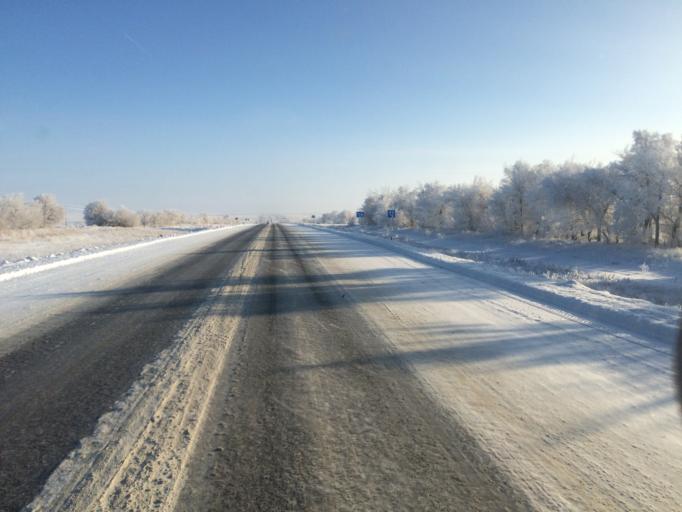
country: KZ
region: Aqtoebe
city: Martuk
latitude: 50.1865
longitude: 55.8130
